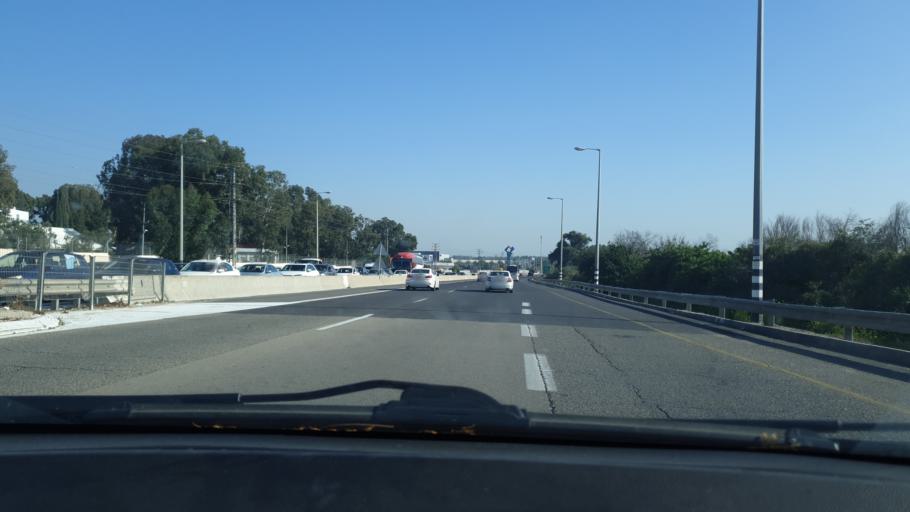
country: IL
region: Central District
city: Kefar Habad
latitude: 31.9684
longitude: 34.8445
